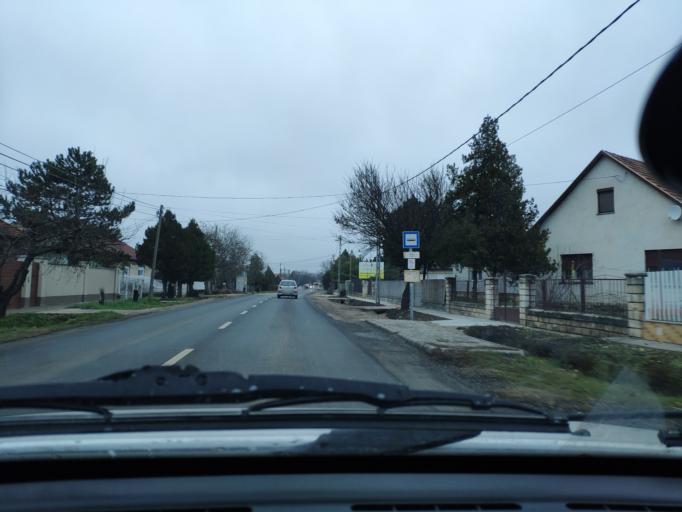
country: HU
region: Pest
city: Soskut
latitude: 47.3999
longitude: 18.8382
